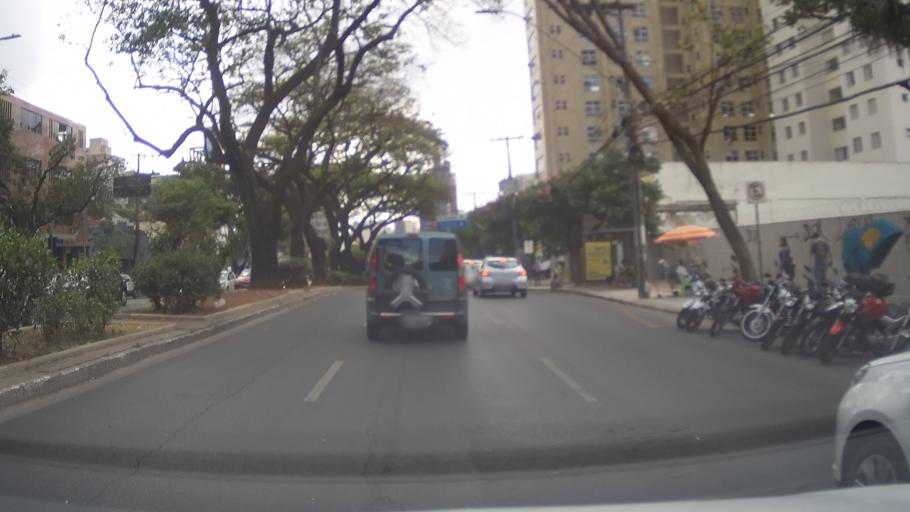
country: BR
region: Minas Gerais
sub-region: Belo Horizonte
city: Belo Horizonte
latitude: -19.9223
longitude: -43.9204
